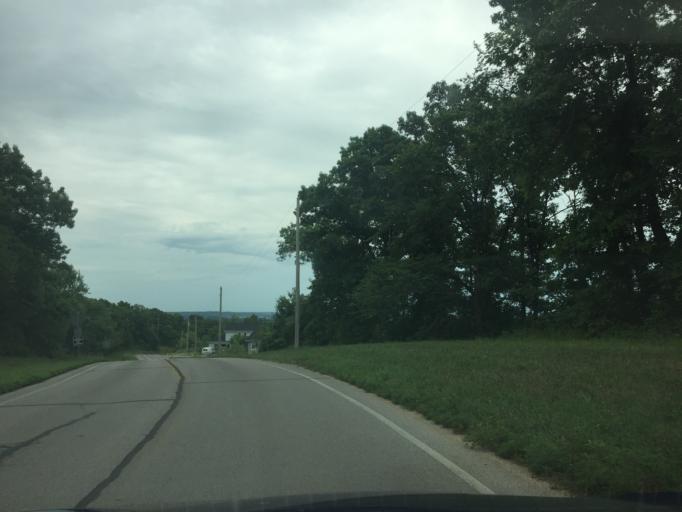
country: US
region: Kansas
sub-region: Leavenworth County
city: Leavenworth
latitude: 39.3510
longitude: -94.9409
